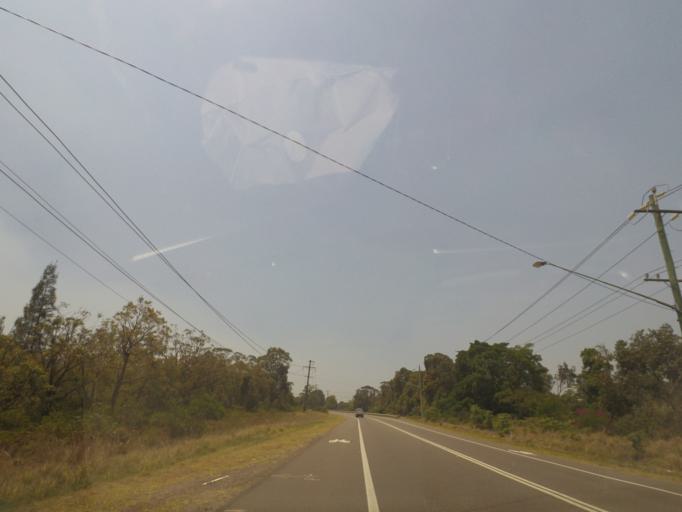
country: AU
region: New South Wales
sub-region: Newcastle
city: Mayfield West
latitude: -32.8317
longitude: 151.7189
